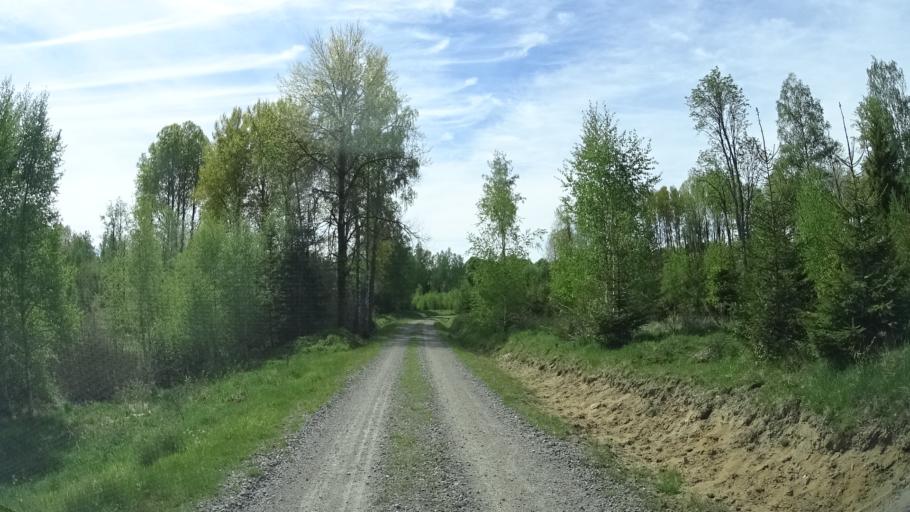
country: SE
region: OEstergoetland
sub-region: Finspangs Kommun
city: Finspang
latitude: 58.8021
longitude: 15.8385
